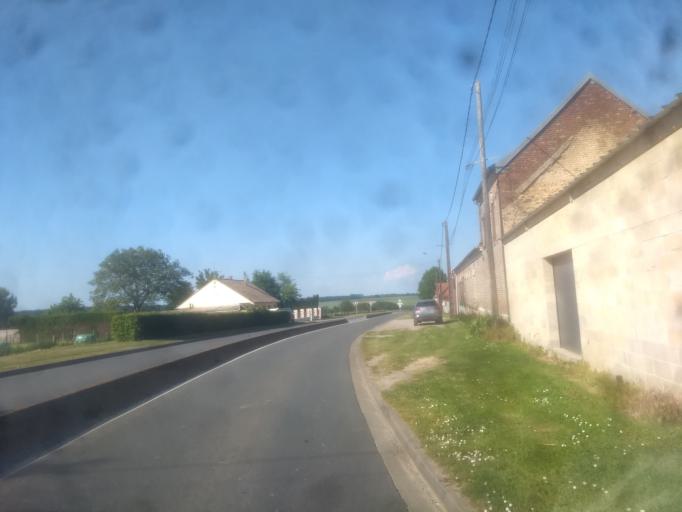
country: FR
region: Picardie
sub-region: Departement de la Somme
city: Doullens
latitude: 50.1549
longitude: 2.2852
